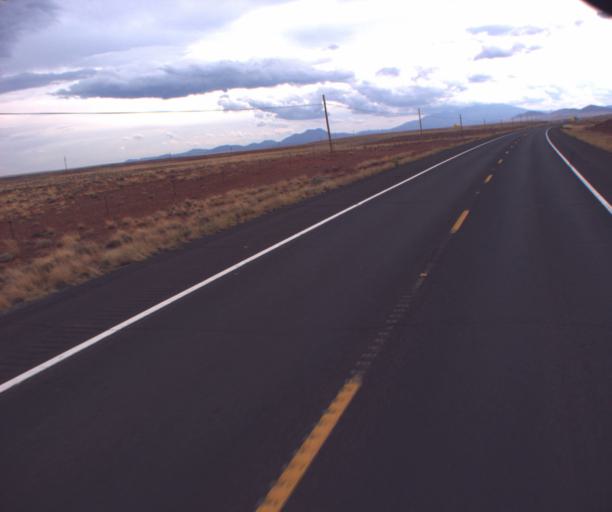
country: US
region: Arizona
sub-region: Coconino County
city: Tuba City
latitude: 35.7207
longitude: -111.4852
